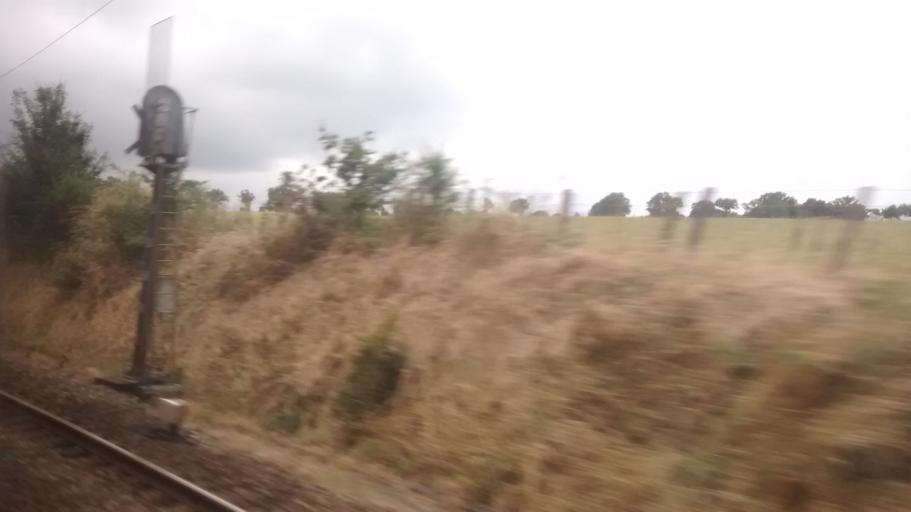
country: FR
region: Pays de la Loire
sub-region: Departement de la Mayenne
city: Louverne
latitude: 48.1173
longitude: -0.6982
